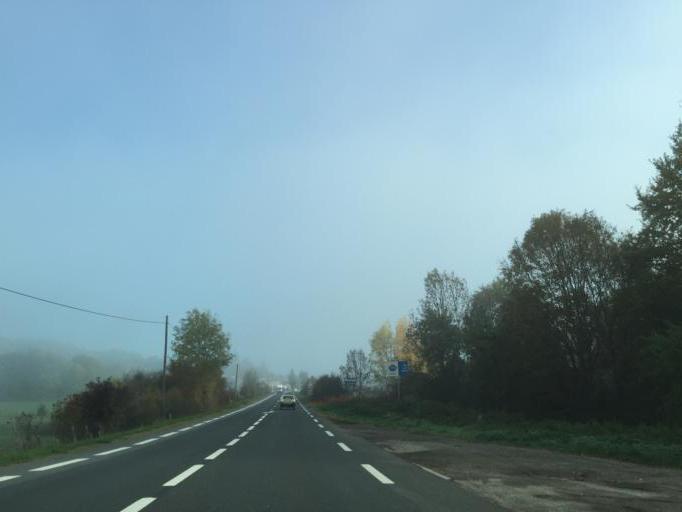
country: FR
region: Rhone-Alpes
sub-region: Departement du Rhone
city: Montagny
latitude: 45.6492
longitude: 4.7471
